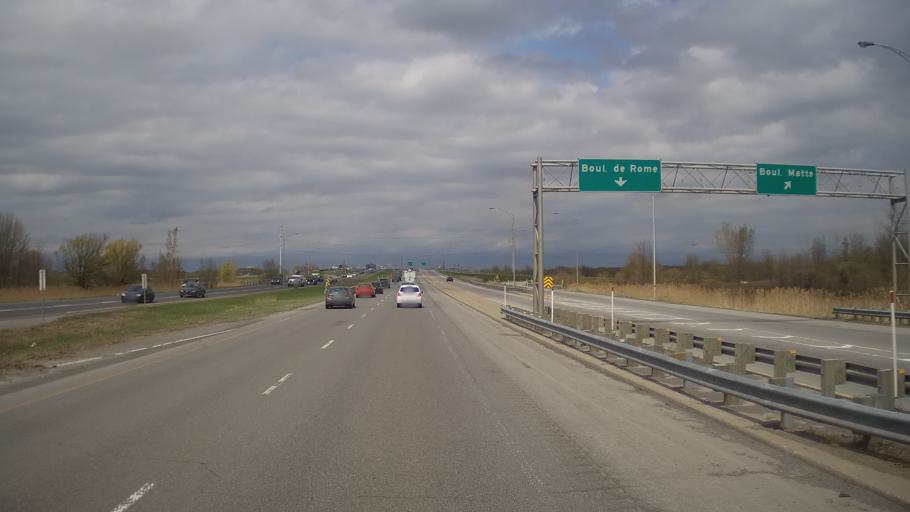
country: CA
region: Quebec
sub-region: Monteregie
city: Brossard
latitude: 45.4182
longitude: -73.4518
